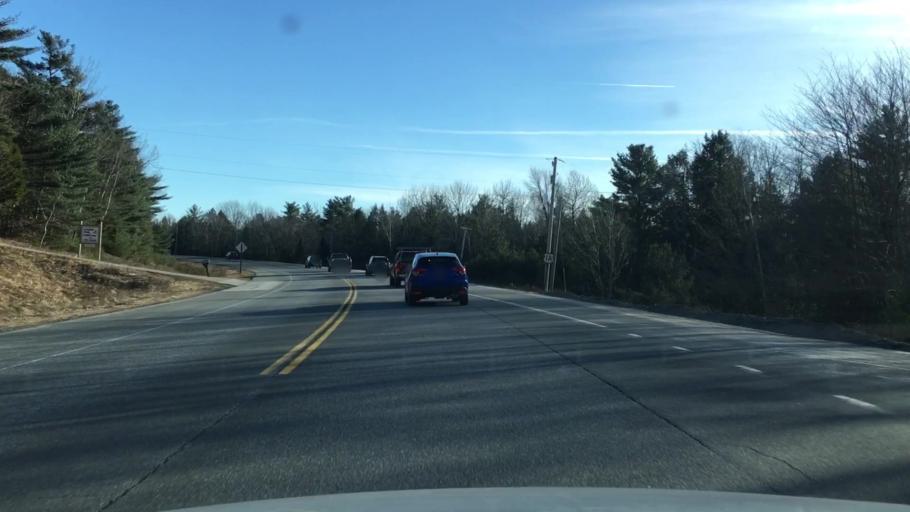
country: US
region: Maine
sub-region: Hancock County
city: Dedham
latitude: 44.6704
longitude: -68.5763
